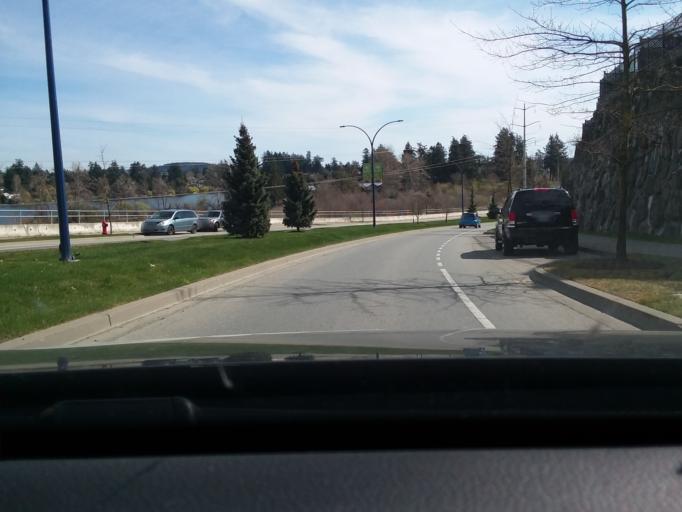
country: CA
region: British Columbia
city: Langford
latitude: 48.4453
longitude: -123.5326
